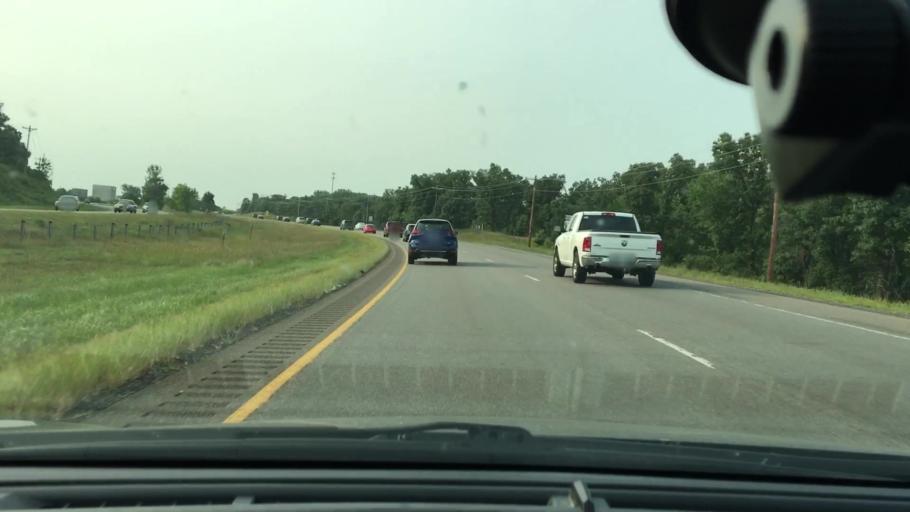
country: US
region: Minnesota
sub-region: Sherburne County
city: Elk River
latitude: 45.3518
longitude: -93.5581
